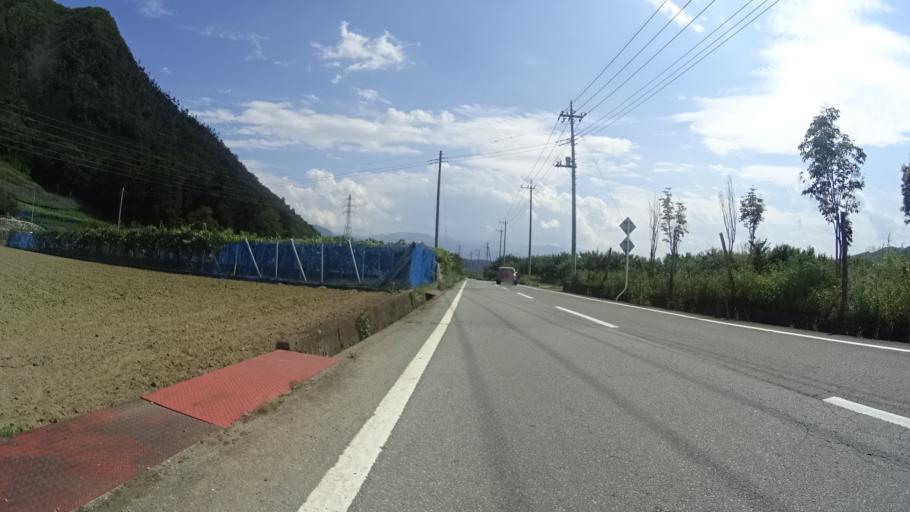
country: JP
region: Yamanashi
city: Enzan
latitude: 35.7388
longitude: 138.7213
